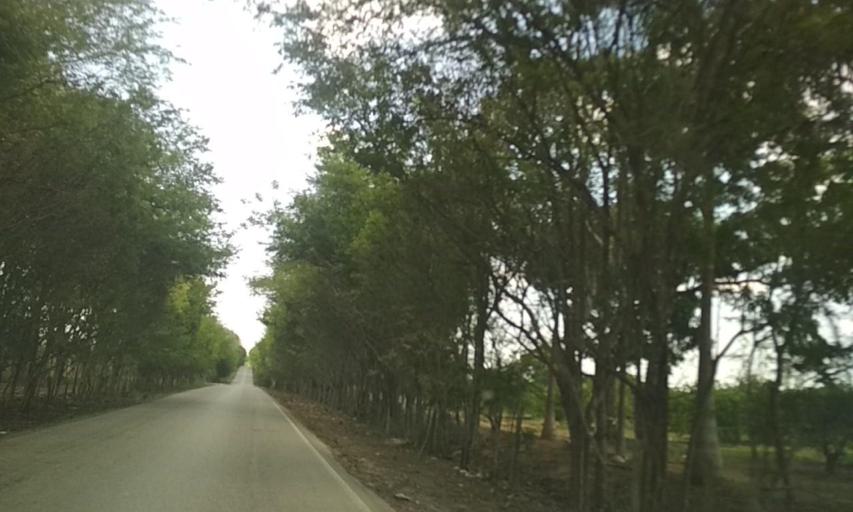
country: MX
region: Tabasco
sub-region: Huimanguillo
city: Paso de la Mina 2da. Seccion (Barrial)
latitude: 17.7712
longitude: -93.6454
